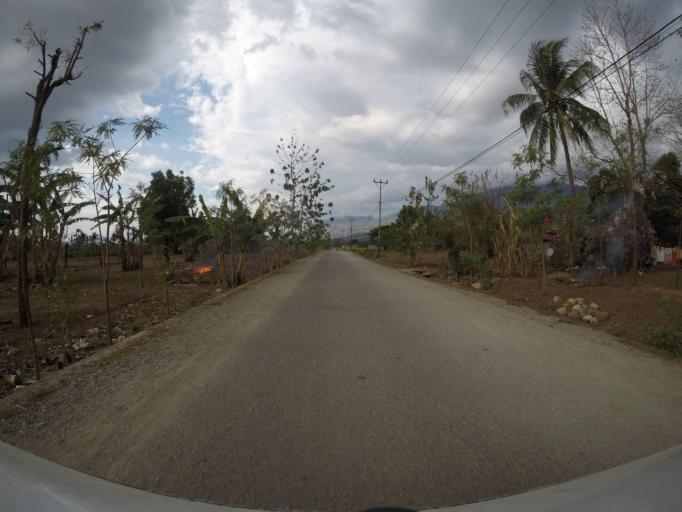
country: TL
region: Bobonaro
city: Maliana
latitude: -8.9878
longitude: 125.2088
